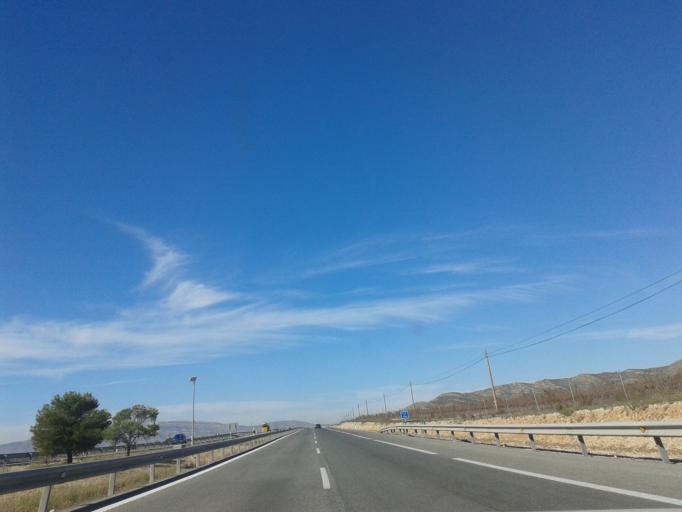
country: ES
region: Valencia
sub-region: Provincia de Alicante
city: Villena
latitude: 38.6782
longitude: -0.8952
